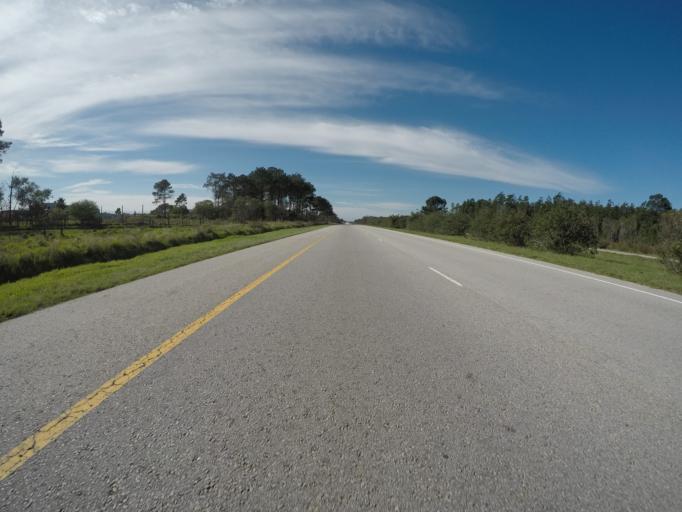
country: ZA
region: Eastern Cape
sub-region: Nelson Mandela Bay Metropolitan Municipality
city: Uitenhage
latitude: -33.9217
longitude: 25.3052
